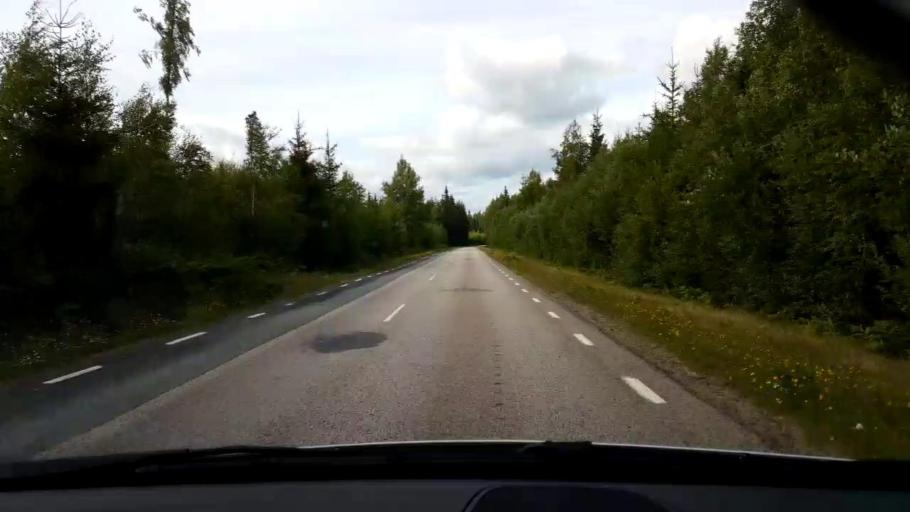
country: SE
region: Joenkoeping
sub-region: Vetlanda Kommun
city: Vetlanda
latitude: 57.3441
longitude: 15.0743
